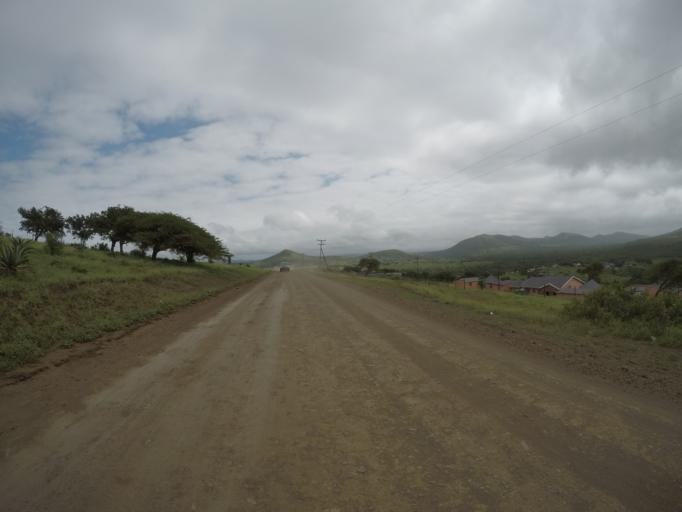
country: ZA
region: KwaZulu-Natal
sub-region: uThungulu District Municipality
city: Empangeni
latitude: -28.6255
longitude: 31.8701
